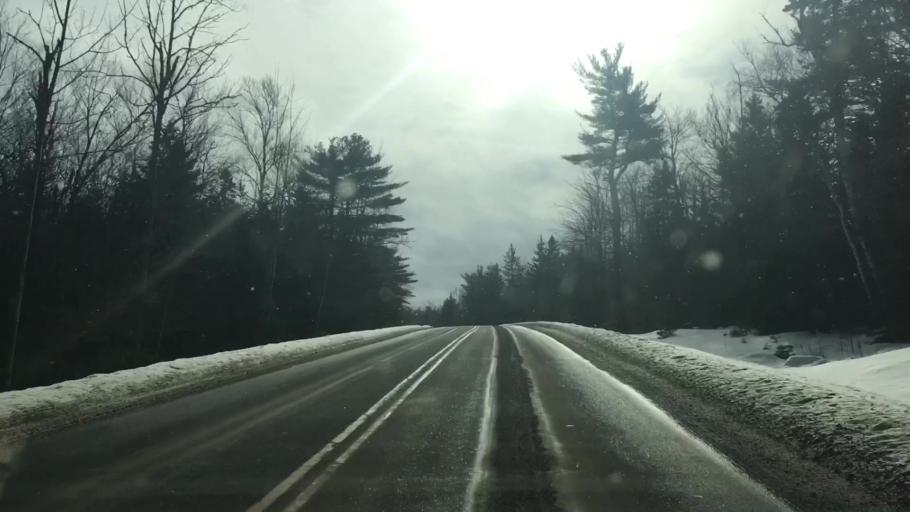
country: US
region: Maine
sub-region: Washington County
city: Calais
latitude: 45.0657
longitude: -67.3300
